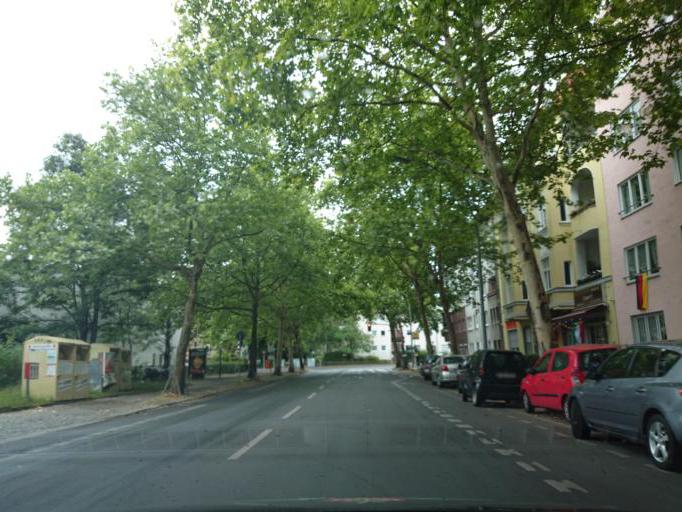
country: DE
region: Berlin
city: Steglitz Bezirk
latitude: 52.4432
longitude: 13.3316
